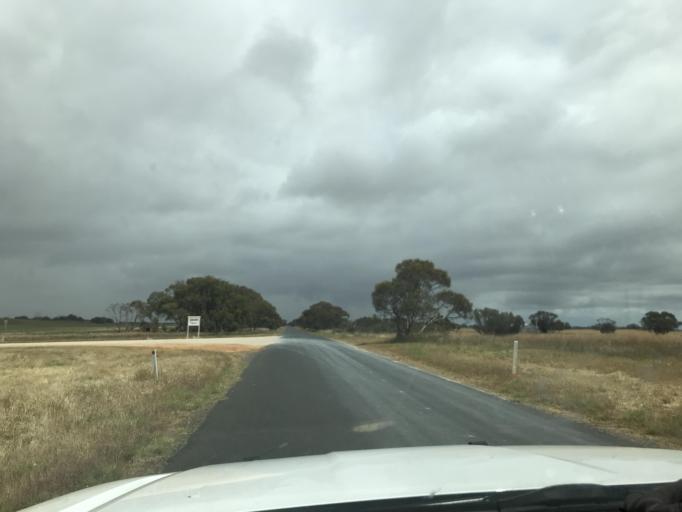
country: AU
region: South Australia
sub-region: Tatiara
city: Bordertown
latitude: -36.1216
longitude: 141.0725
